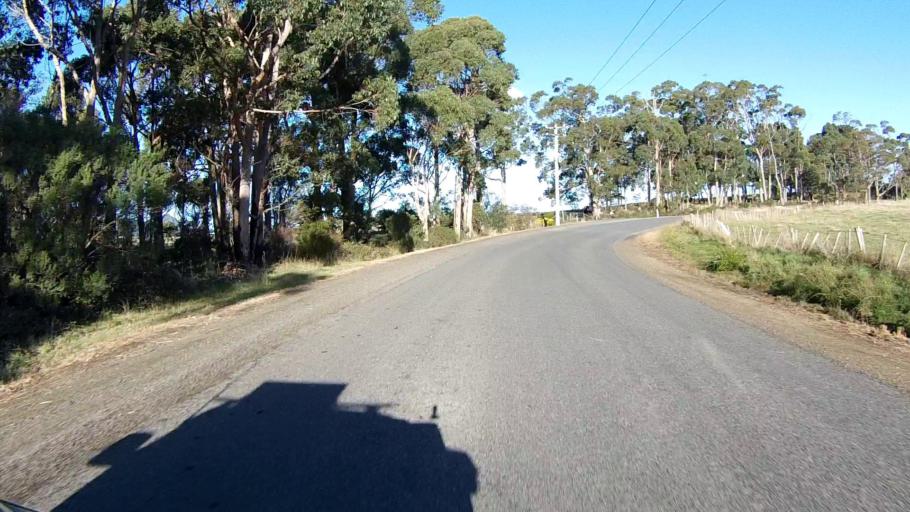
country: AU
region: Tasmania
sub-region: Clarence
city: Sandford
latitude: -43.1663
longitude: 147.8598
